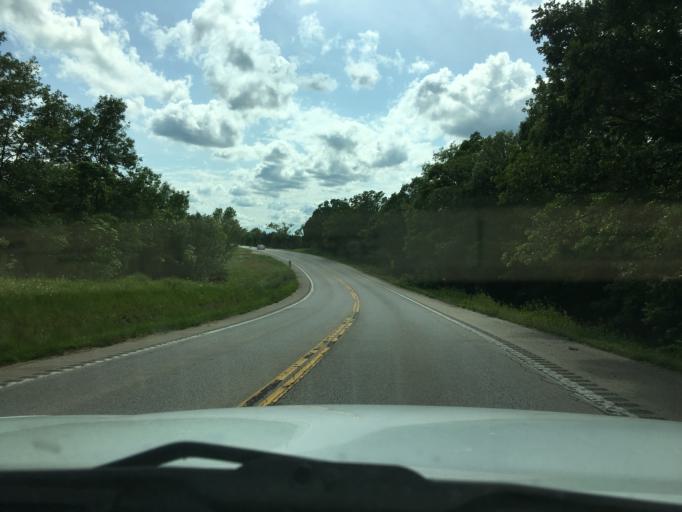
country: US
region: Missouri
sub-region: Franklin County
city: Gerald
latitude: 38.3959
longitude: -91.3526
